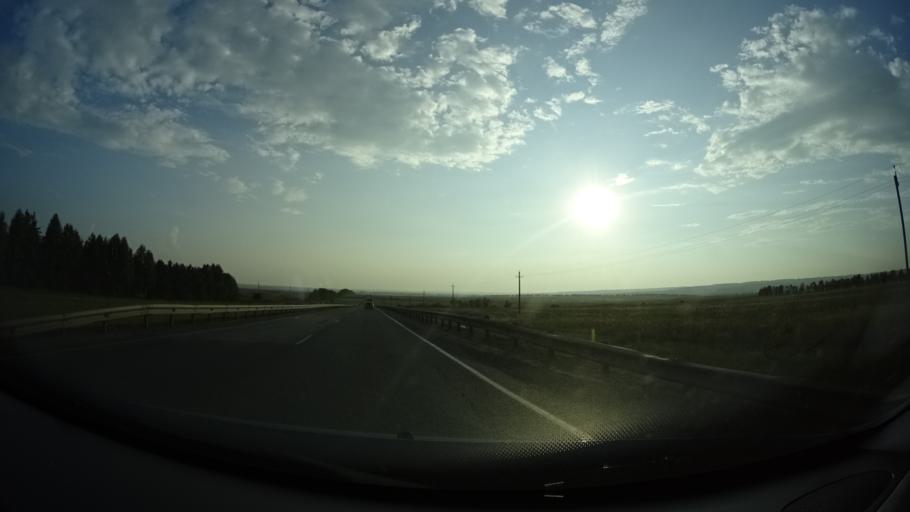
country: RU
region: Samara
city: Kamyshla
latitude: 54.0567
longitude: 52.0744
